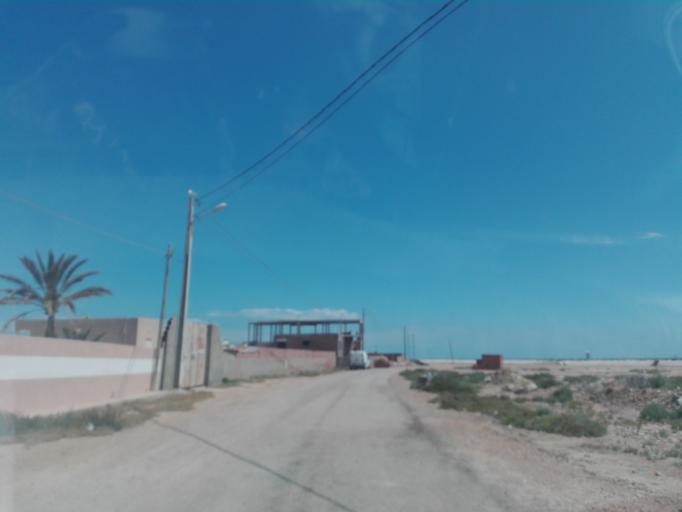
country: TN
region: Safaqis
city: Jabinyanah
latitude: 34.8174
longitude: 11.2632
